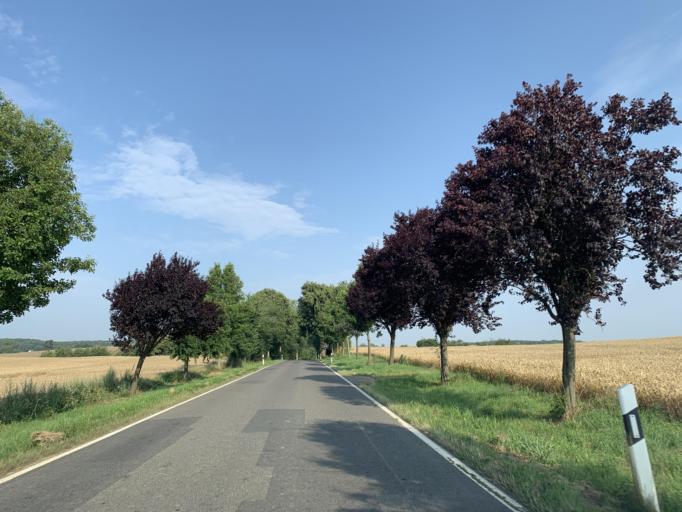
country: DE
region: Mecklenburg-Vorpommern
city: Gross Nemerow
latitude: 53.4209
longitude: 13.2107
